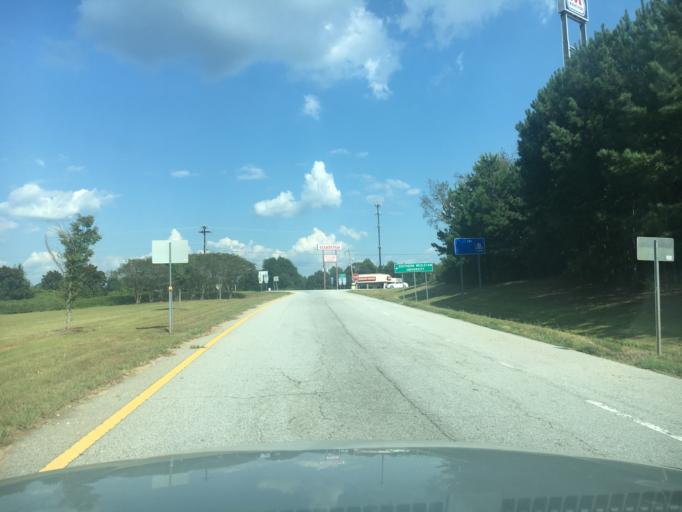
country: US
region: South Carolina
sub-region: Anderson County
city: Centerville
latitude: 34.5460
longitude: -82.8081
